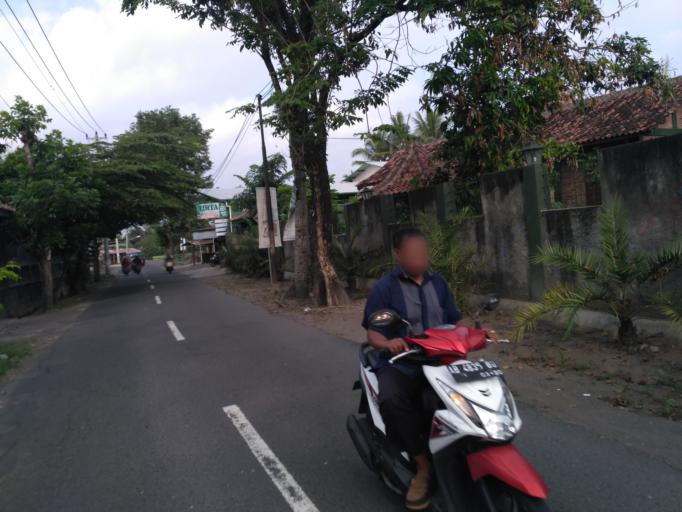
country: ID
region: Daerah Istimewa Yogyakarta
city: Melati
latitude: -7.7096
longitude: 110.3912
